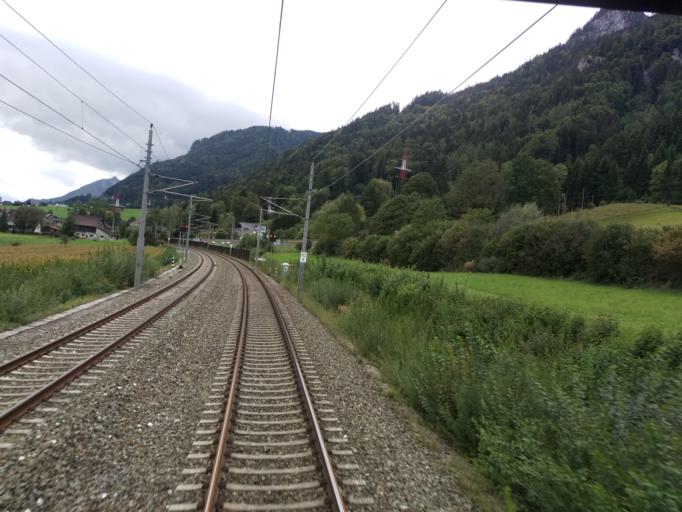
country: AT
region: Styria
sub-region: Politischer Bezirk Liezen
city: Stainach
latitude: 47.5444
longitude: 14.1275
